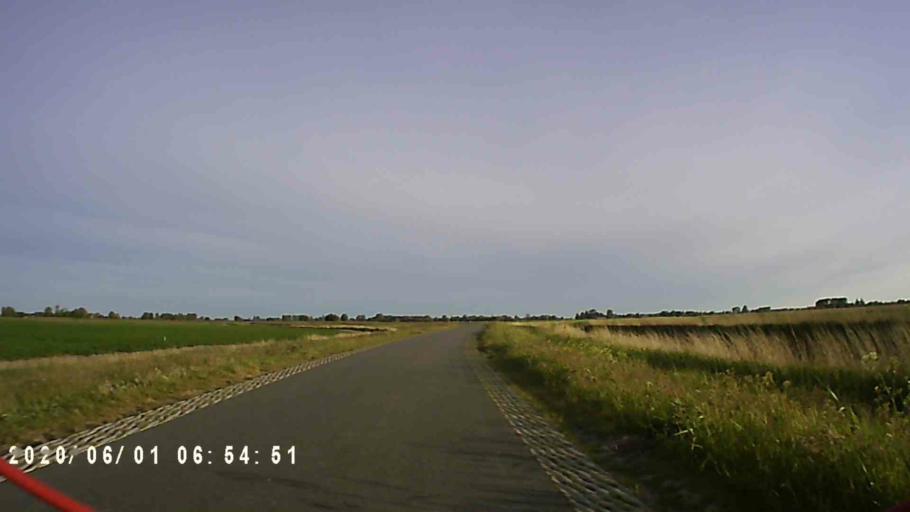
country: NL
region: Friesland
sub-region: Gemeente Kollumerland en Nieuwkruisland
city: Kollum
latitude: 53.3147
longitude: 6.1217
